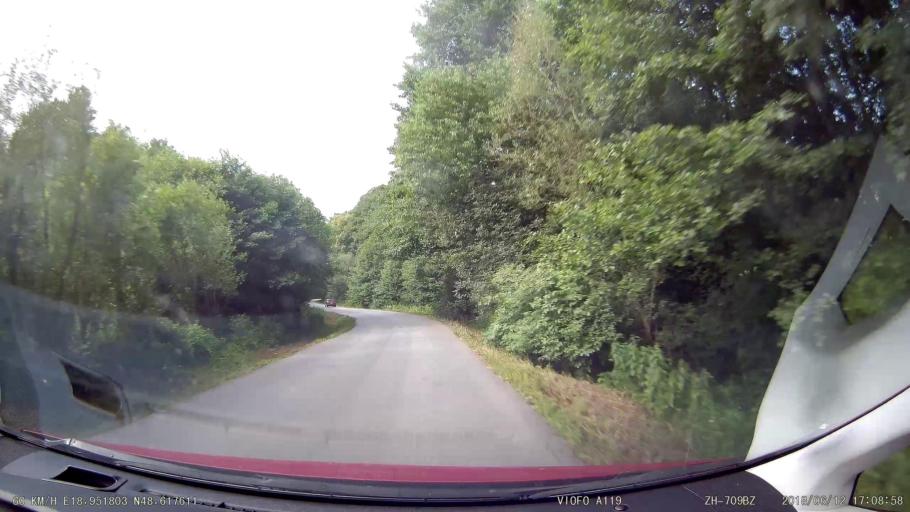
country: SK
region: Banskobystricky
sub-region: Okres Ziar nad Hronom
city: Kremnica
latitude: 48.6178
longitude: 18.9519
